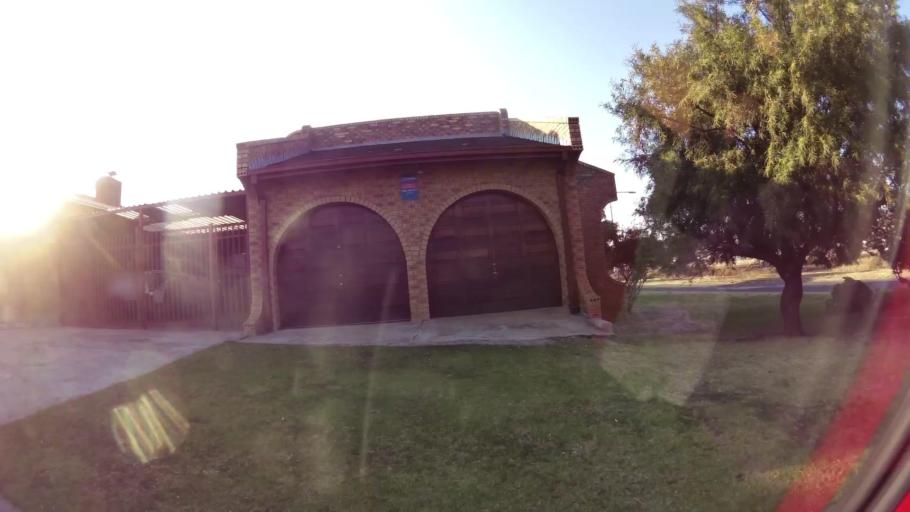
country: ZA
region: Gauteng
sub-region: City of Johannesburg Metropolitan Municipality
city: Soweto
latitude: -26.2561
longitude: 27.9559
